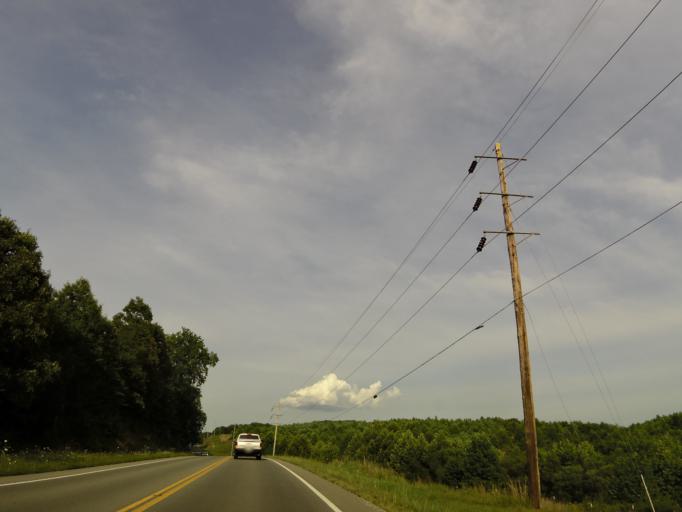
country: US
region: Tennessee
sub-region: Humphreys County
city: McEwen
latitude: 36.0927
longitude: -87.5520
